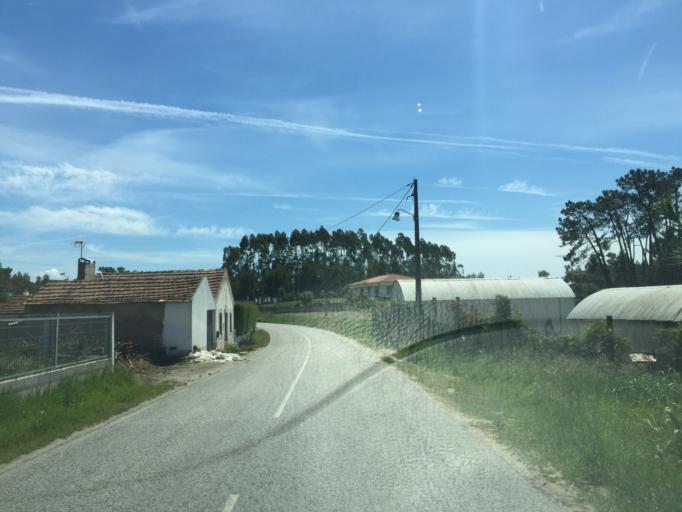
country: PT
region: Coimbra
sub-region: Figueira da Foz
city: Lavos
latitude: 40.0711
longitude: -8.7702
